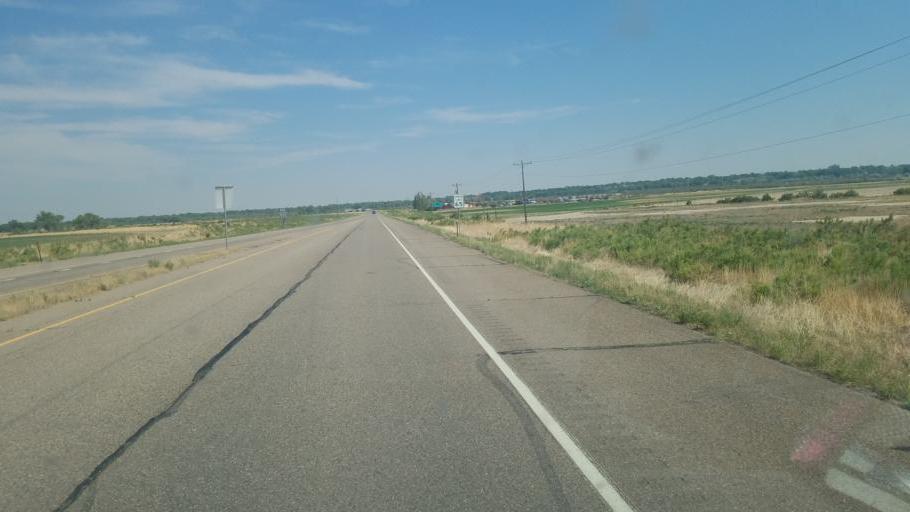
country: US
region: Colorado
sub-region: Pueblo County
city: Pueblo
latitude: 38.2596
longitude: -104.3651
